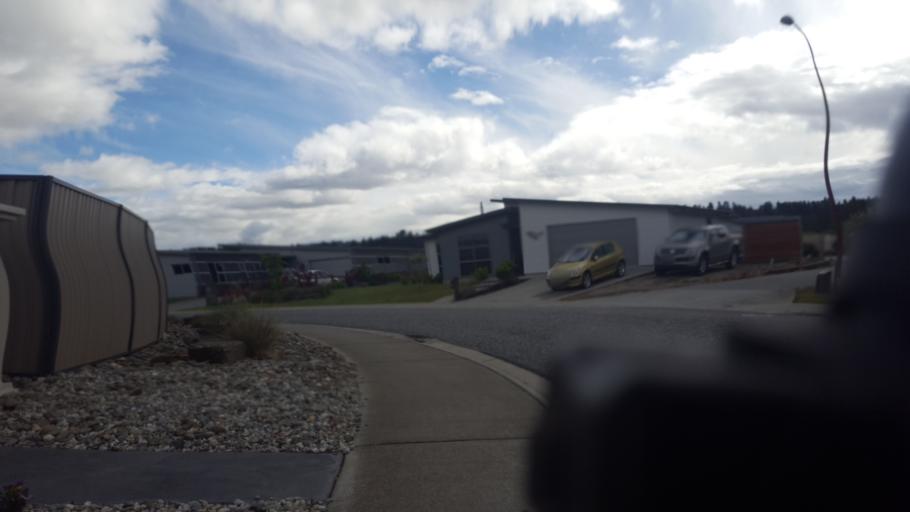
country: NZ
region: Otago
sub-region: Queenstown-Lakes District
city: Wanaka
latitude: -45.2401
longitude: 169.3820
